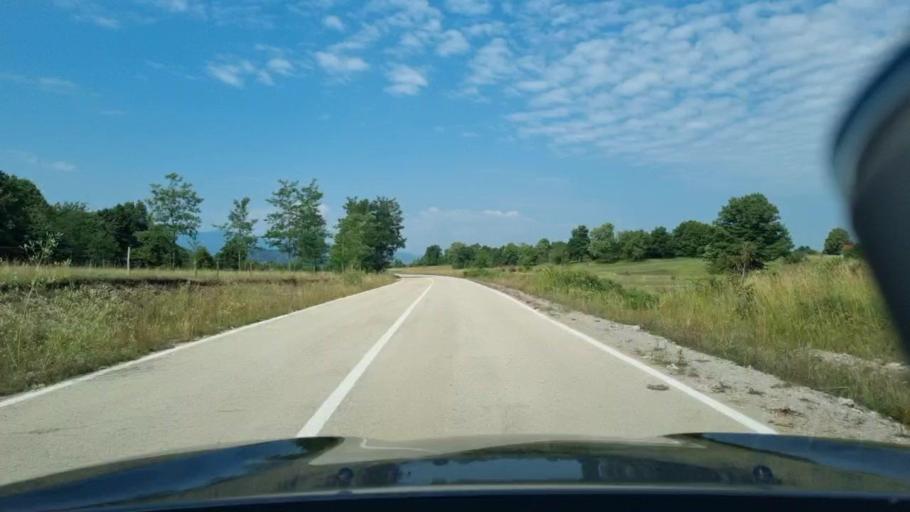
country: BA
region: Federation of Bosnia and Herzegovina
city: Ostrozac
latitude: 44.8932
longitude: 15.9670
